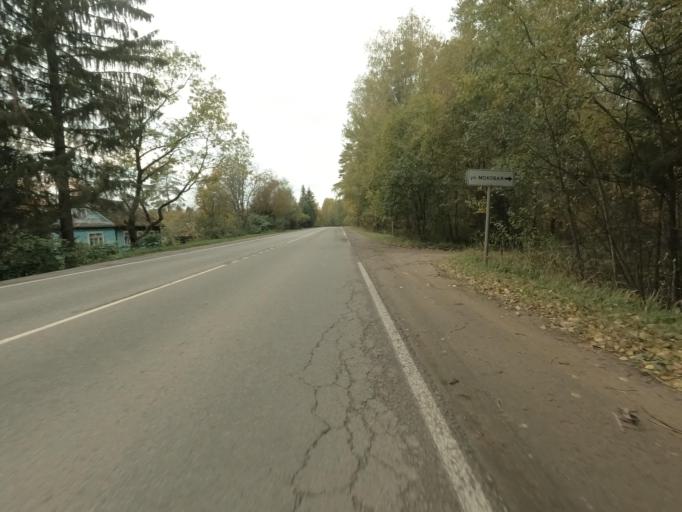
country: RU
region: Leningrad
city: Pavlovo
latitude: 59.7892
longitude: 30.9621
